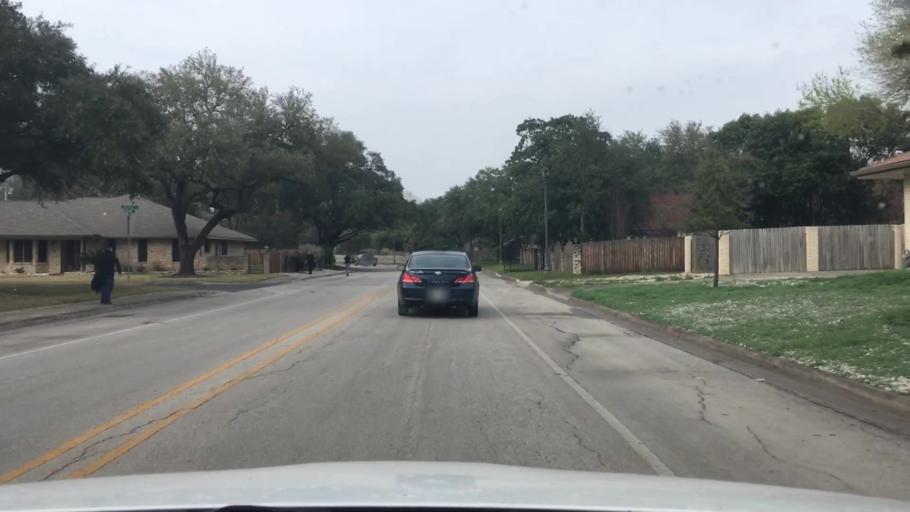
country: US
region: Texas
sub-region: Bexar County
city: Windcrest
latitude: 29.5149
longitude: -98.3804
